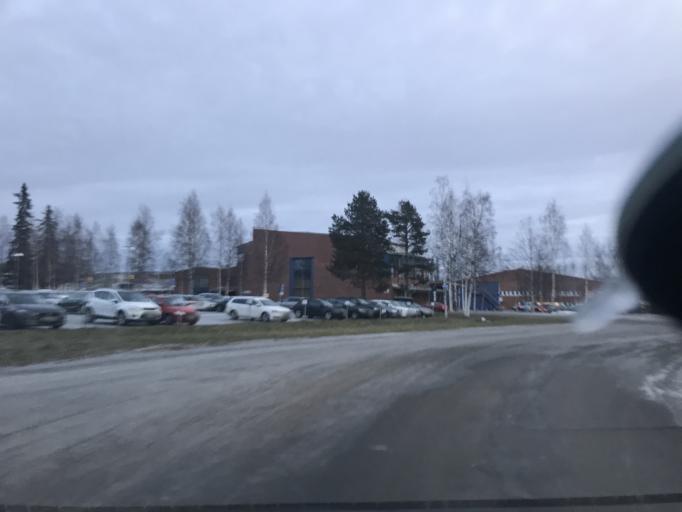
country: SE
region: Norrbotten
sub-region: Lulea Kommun
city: Lulea
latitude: 65.6188
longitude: 22.1320
